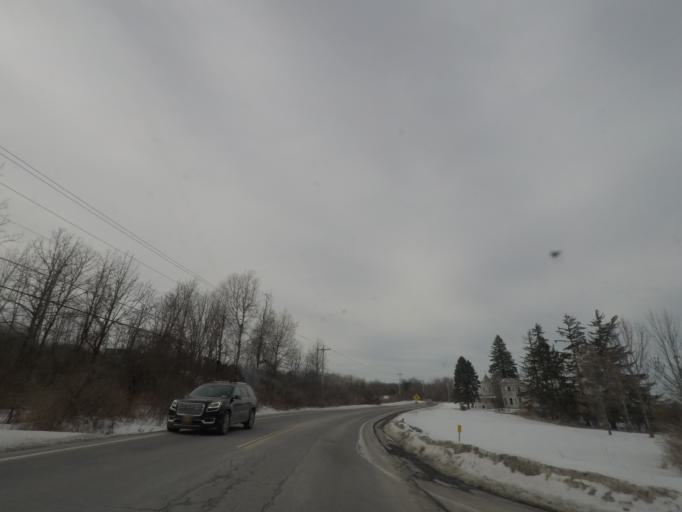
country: US
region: New York
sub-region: Albany County
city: Altamont
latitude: 42.6782
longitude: -74.0863
